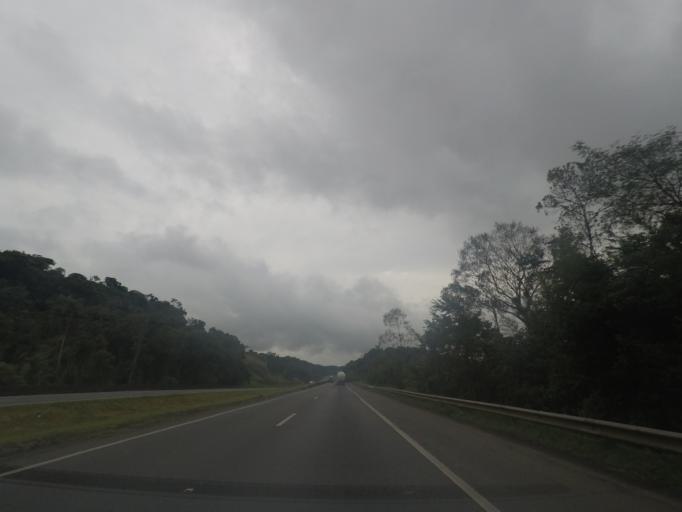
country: BR
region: Sao Paulo
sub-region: Cajati
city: Cajati
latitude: -24.9588
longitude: -48.3358
